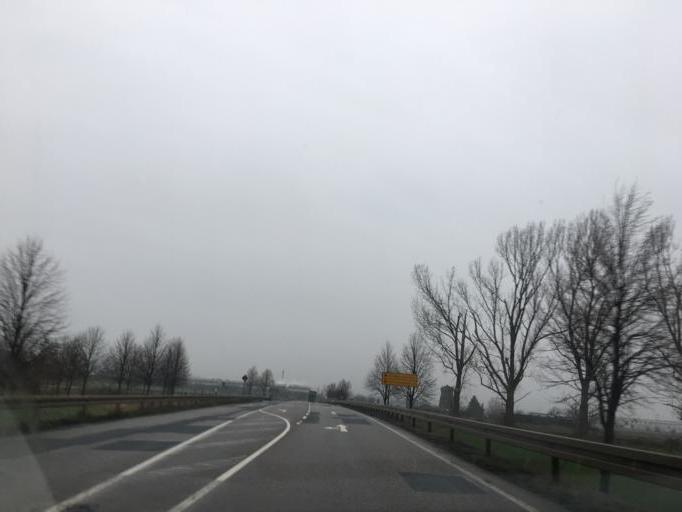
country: DE
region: Saxony-Anhalt
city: Gross Ammensleben
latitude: 52.2210
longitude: 11.5386
